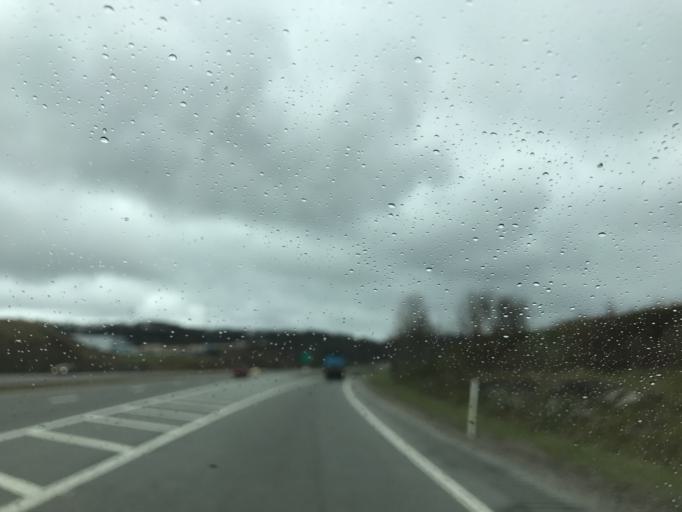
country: US
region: West Virginia
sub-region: Raleigh County
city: Bradley
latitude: 37.8545
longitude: -81.1909
